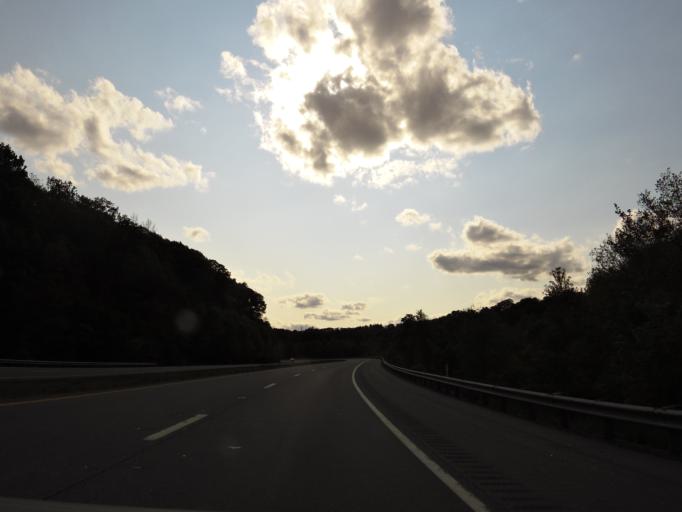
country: US
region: West Virginia
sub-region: Mercer County
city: Princeton
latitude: 37.3533
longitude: -81.1019
